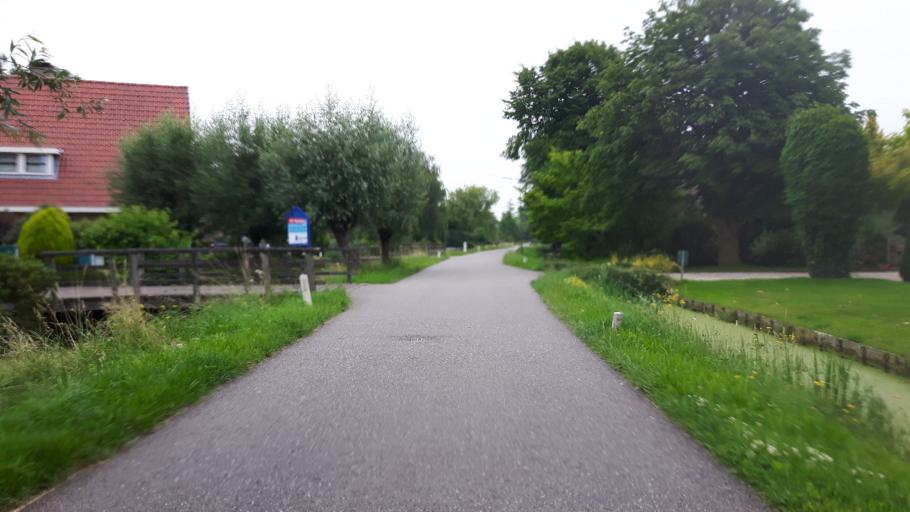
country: NL
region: South Holland
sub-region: Gemeente Schoonhoven
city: Schoonhoven
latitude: 51.9430
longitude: 4.8682
